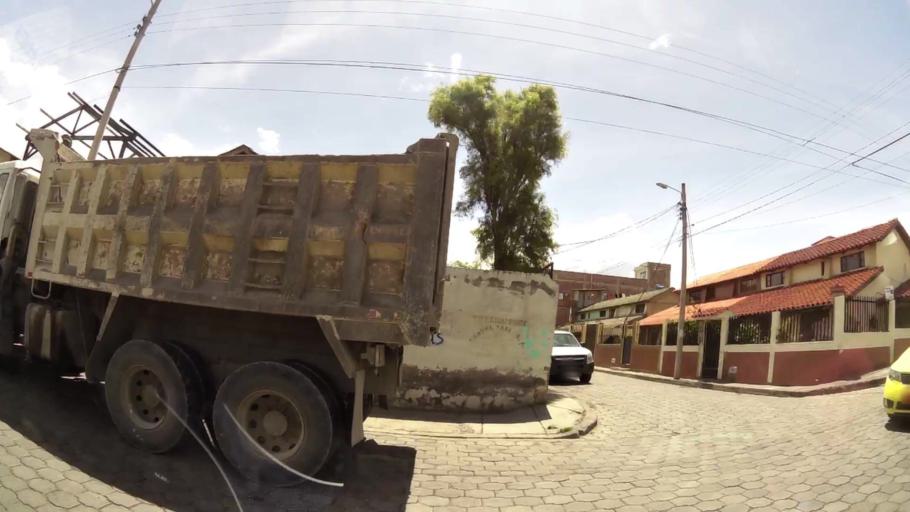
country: EC
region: Chimborazo
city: Riobamba
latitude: -1.6620
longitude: -78.6393
